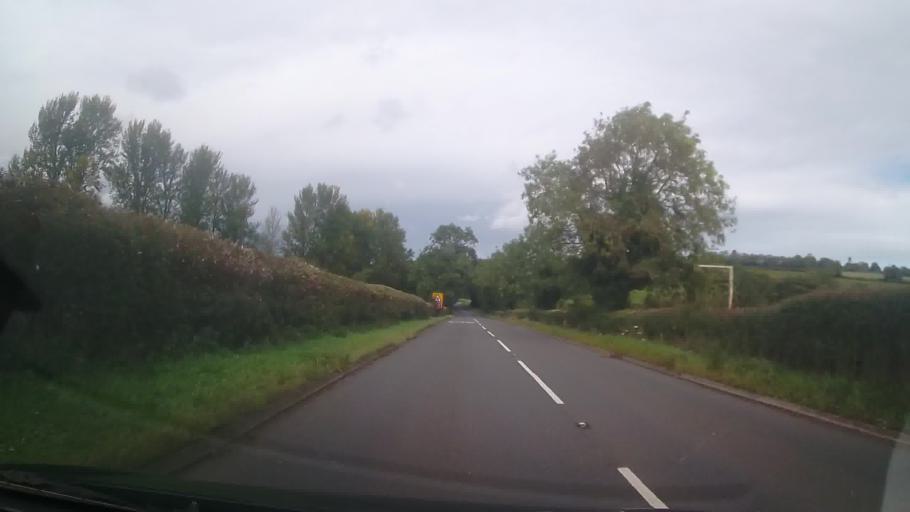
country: GB
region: England
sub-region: Shropshire
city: Alveley
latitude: 52.4655
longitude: -2.3444
